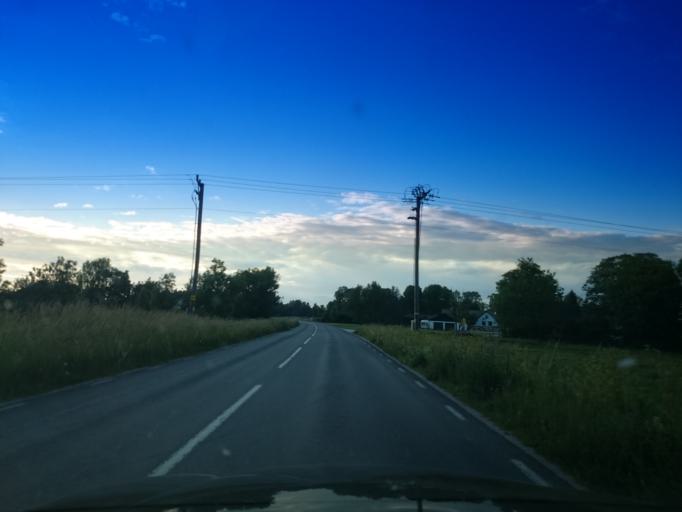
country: SE
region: Gotland
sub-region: Gotland
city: Hemse
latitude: 57.3223
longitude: 18.3845
